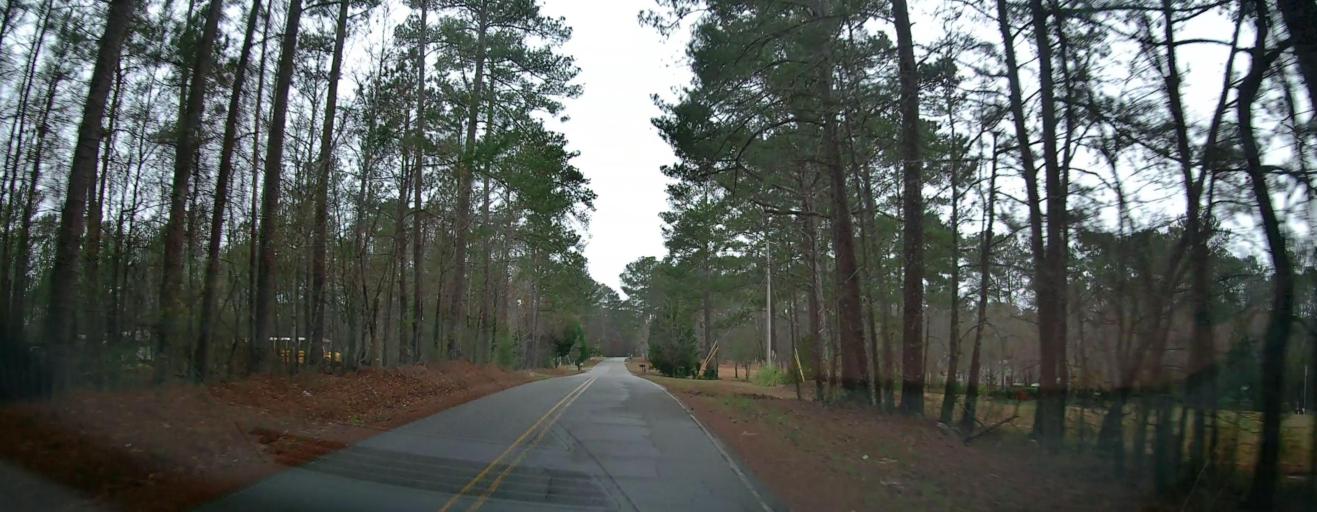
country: US
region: Georgia
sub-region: Monroe County
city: Forsyth
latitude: 33.0186
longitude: -83.8499
